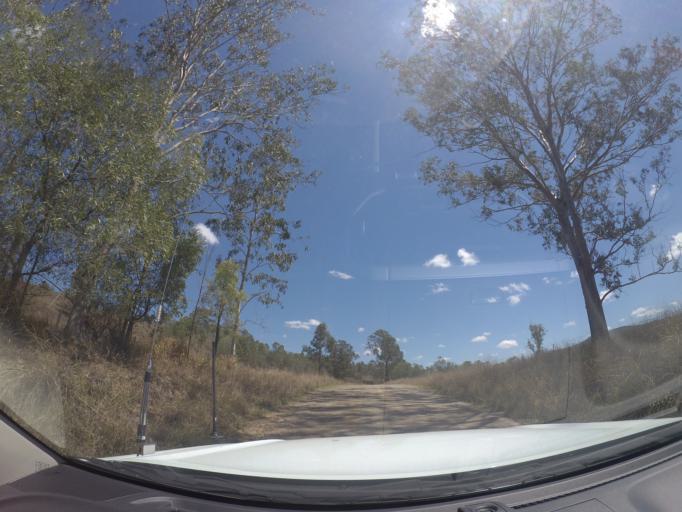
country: AU
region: Queensland
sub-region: Logan
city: North Maclean
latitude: -27.8248
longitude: 152.8605
